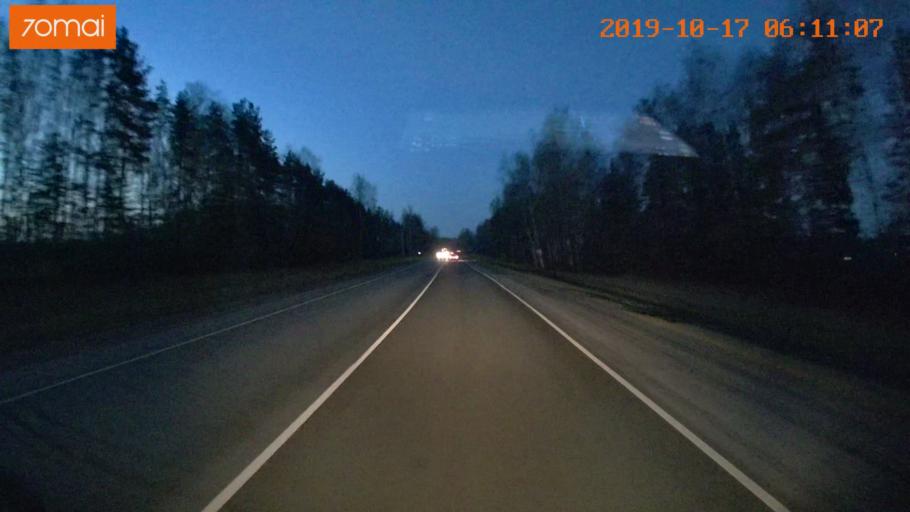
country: RU
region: Ivanovo
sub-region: Gorod Ivanovo
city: Ivanovo
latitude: 56.9238
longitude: 40.9593
